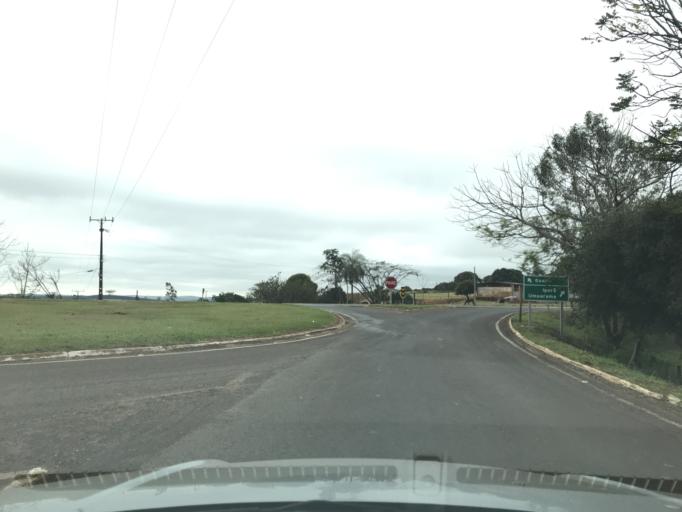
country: BR
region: Parana
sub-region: Ipora
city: Ipora
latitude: -24.0642
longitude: -53.8398
